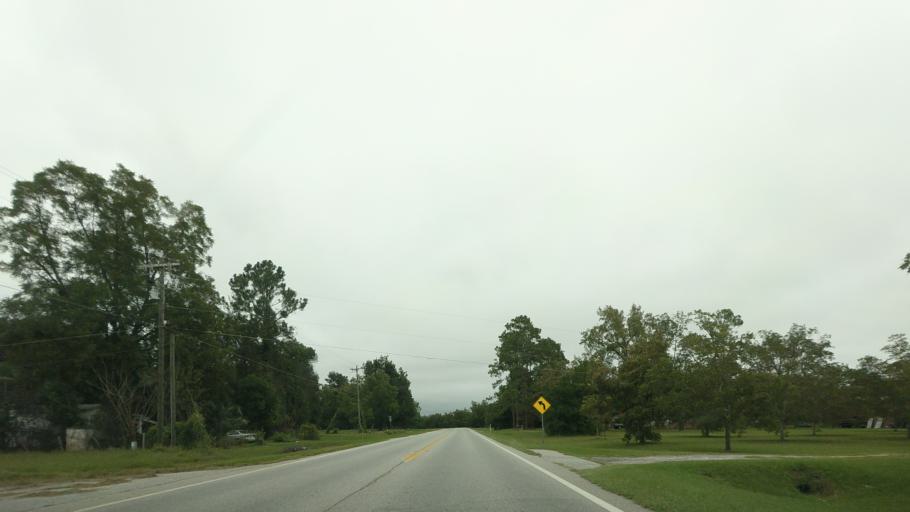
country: US
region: Georgia
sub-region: Berrien County
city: Ray City
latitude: 31.0870
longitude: -83.2057
